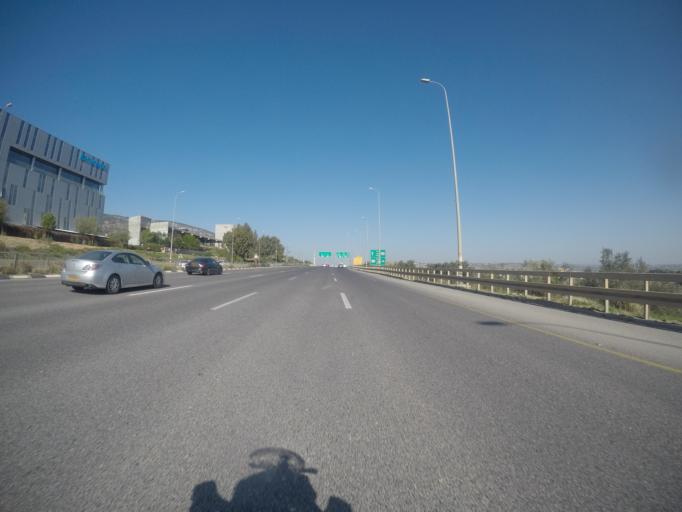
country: IL
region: Haifa
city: Daliyat el Karmil
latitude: 32.6696
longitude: 35.1083
